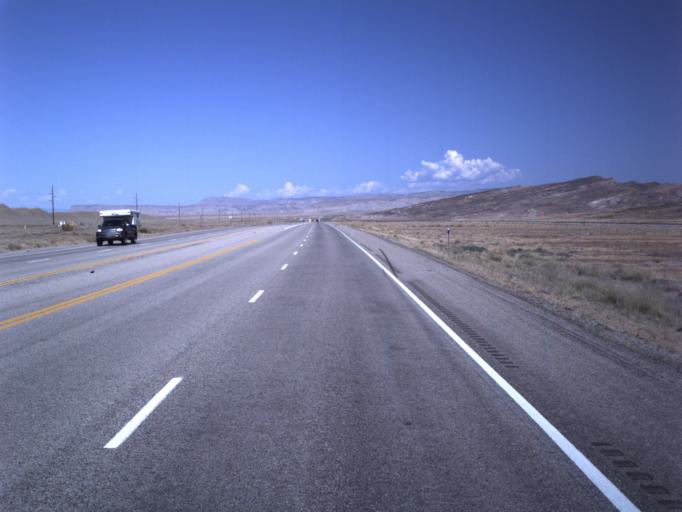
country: US
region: Utah
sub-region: Grand County
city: Moab
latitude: 38.8097
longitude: -109.7702
